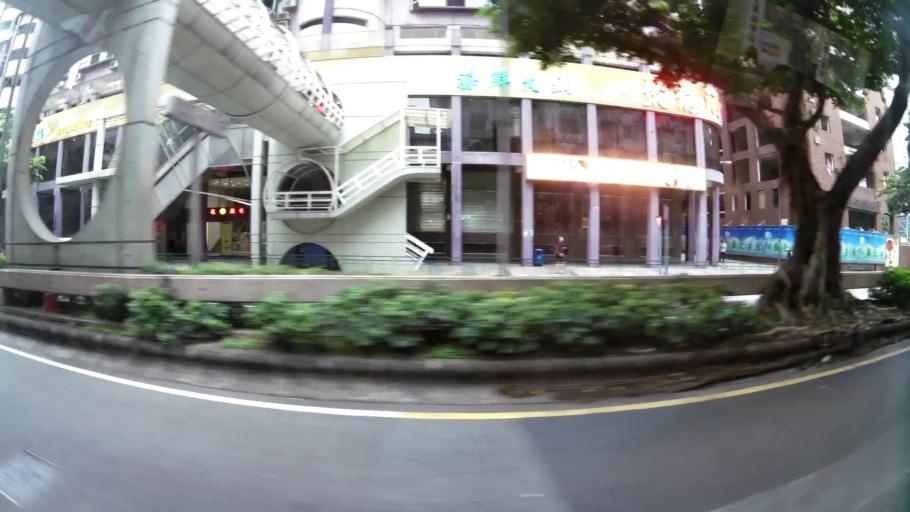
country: MO
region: Macau
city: Macau
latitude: 22.1916
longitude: 113.5459
